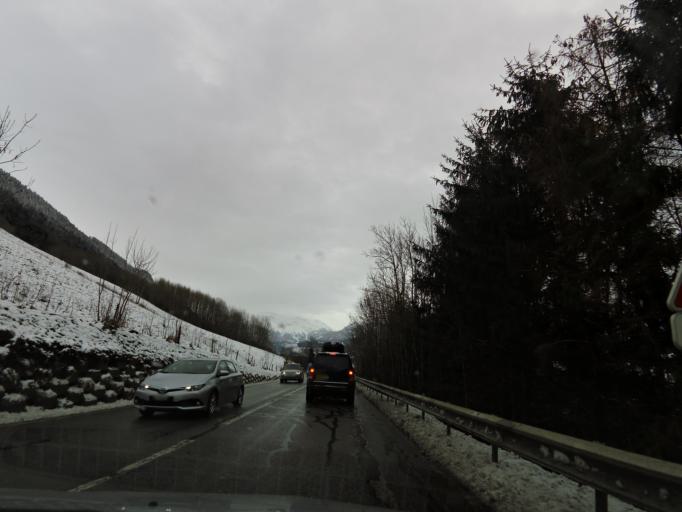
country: FR
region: Rhone-Alpes
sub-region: Departement de la Haute-Savoie
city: Taninges
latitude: 46.1134
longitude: 6.6046
